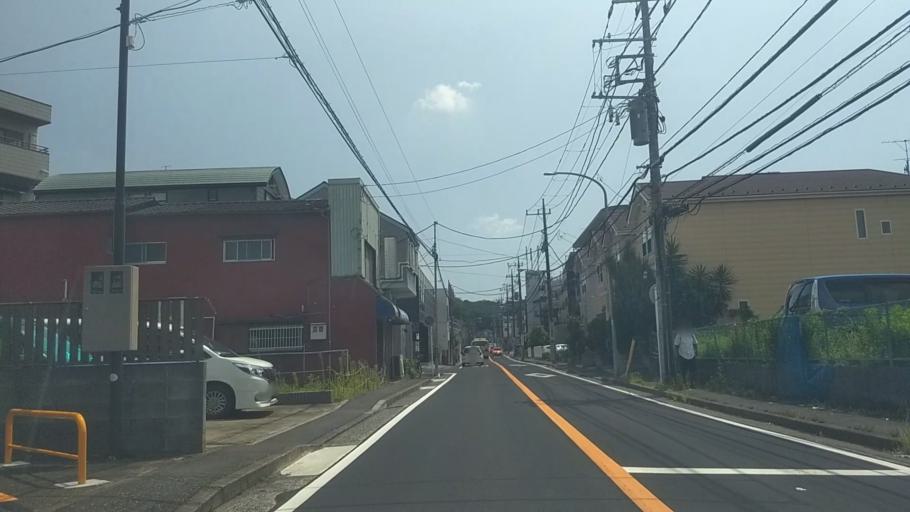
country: JP
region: Kanagawa
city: Yokohama
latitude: 35.5050
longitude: 139.6487
